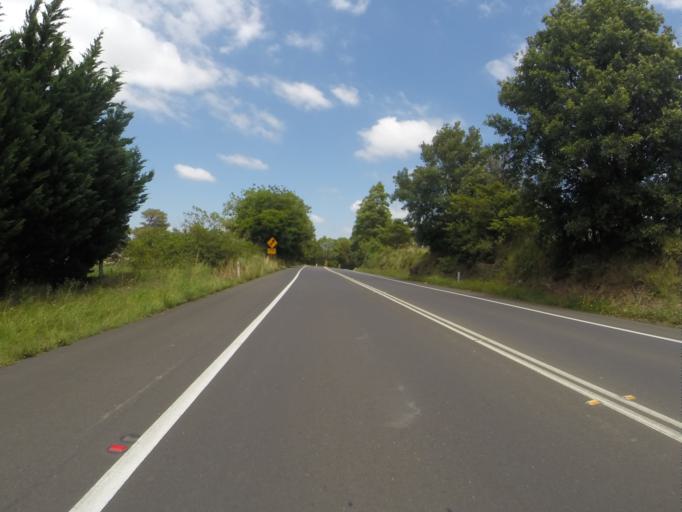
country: AU
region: New South Wales
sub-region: Shoalhaven Shire
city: Berry
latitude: -34.7597
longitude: 150.7404
